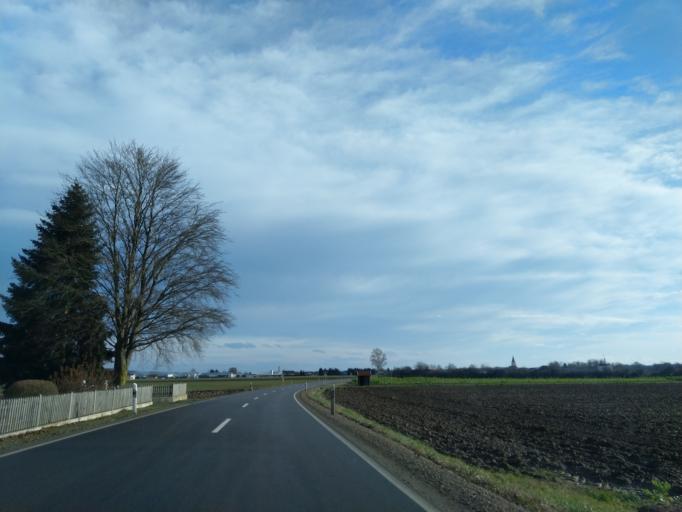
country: DE
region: Bavaria
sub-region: Lower Bavaria
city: Rossbach
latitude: 48.6234
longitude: 12.9707
